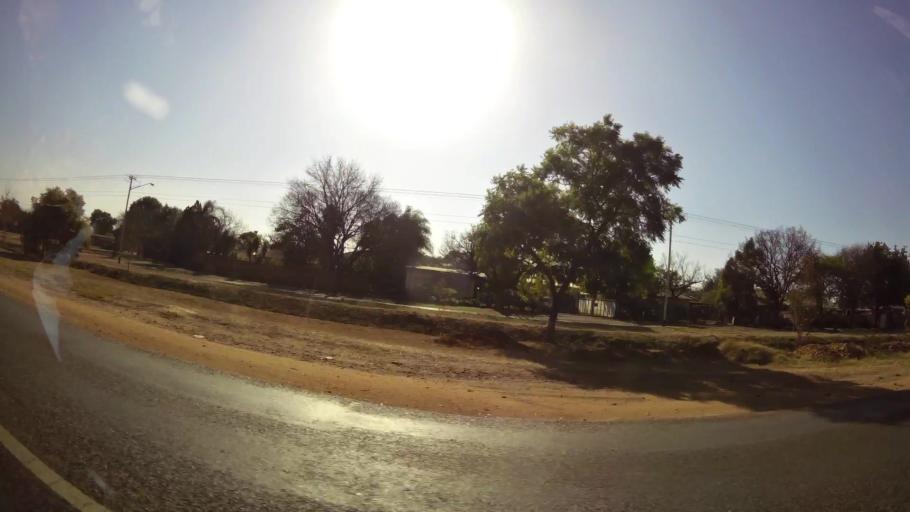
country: ZA
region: Gauteng
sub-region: City of Tshwane Metropolitan Municipality
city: Pretoria
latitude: -25.7147
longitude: 28.2518
